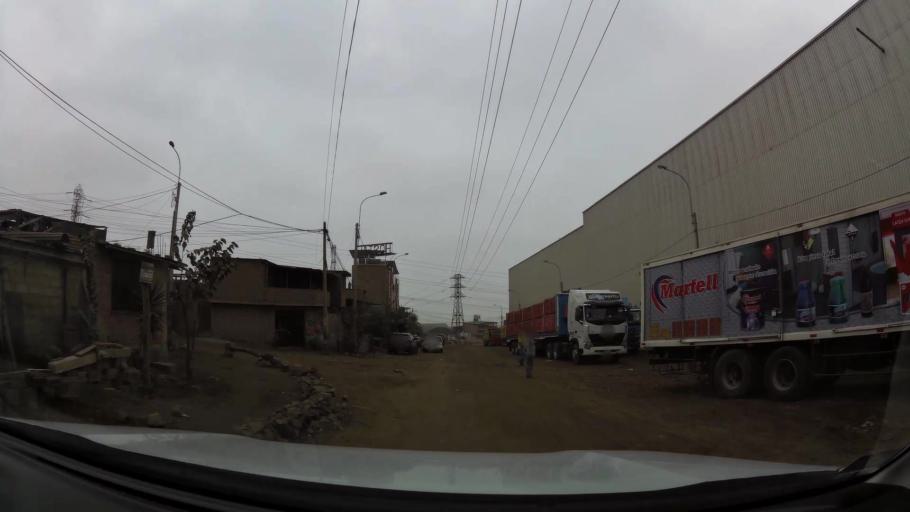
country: PE
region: Lima
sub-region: Lima
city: Surco
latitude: -12.2054
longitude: -76.9267
